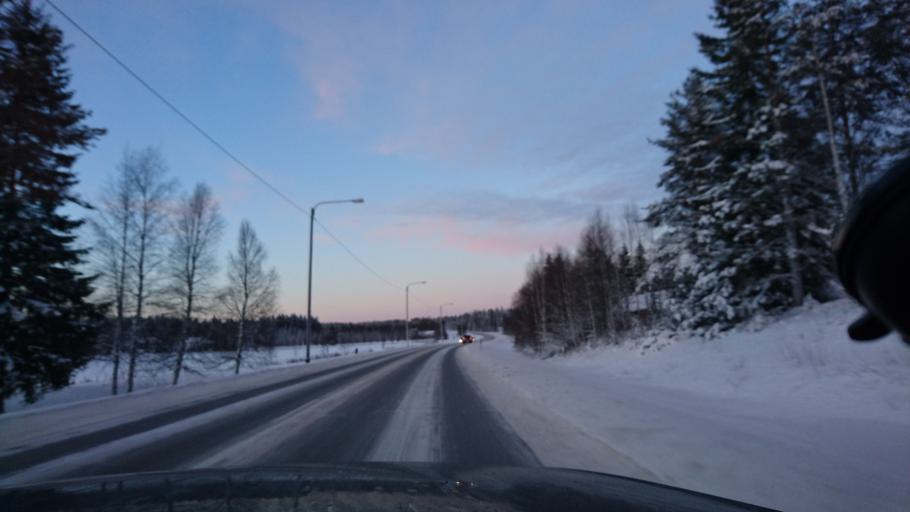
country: FI
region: Lapland
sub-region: Rovaniemi
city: Ranua
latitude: 65.9352
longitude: 26.4932
